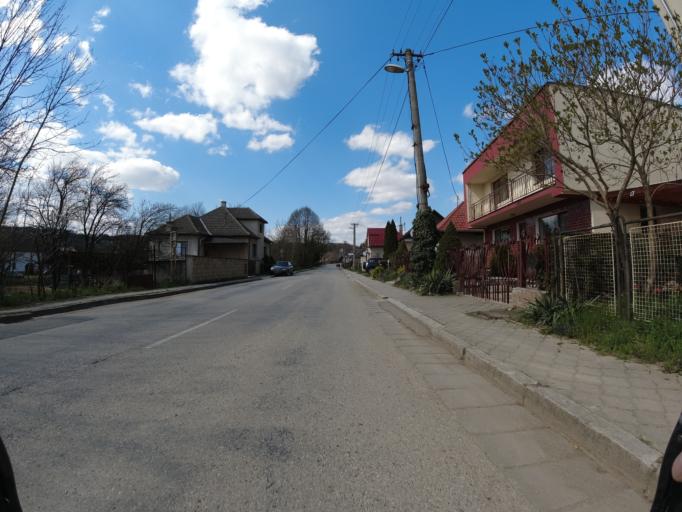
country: SK
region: Nitriansky
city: Stara Tura
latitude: 48.7411
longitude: 17.7233
